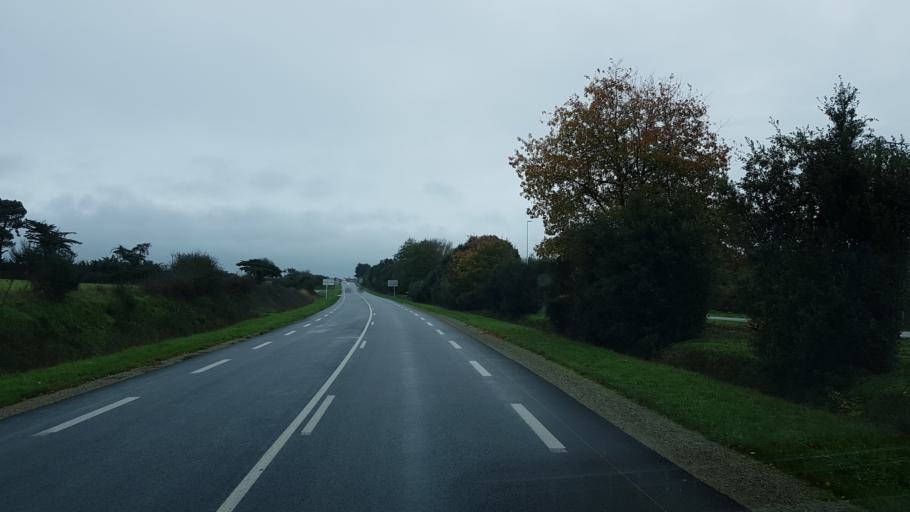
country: FR
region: Brittany
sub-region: Departement du Morbihan
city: Arzon
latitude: 47.5399
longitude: -2.8763
